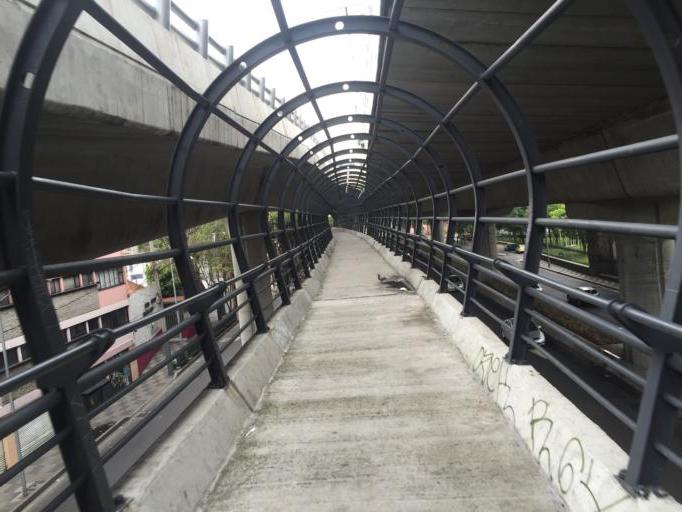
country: MX
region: Mexico City
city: Polanco
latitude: 19.4039
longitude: -99.1923
